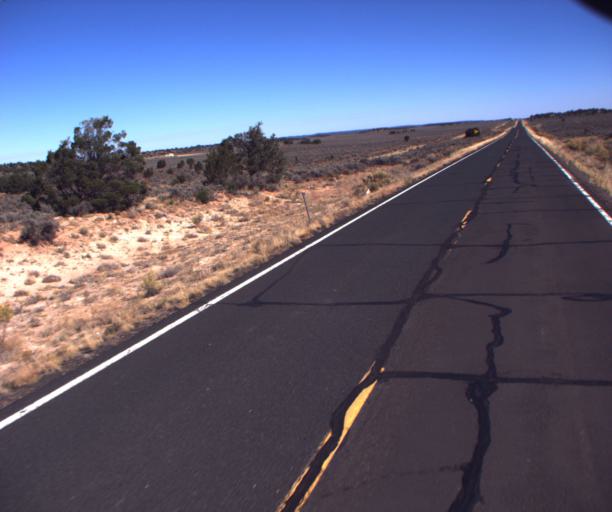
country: US
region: Arizona
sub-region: Navajo County
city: First Mesa
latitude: 35.7413
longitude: -110.0721
